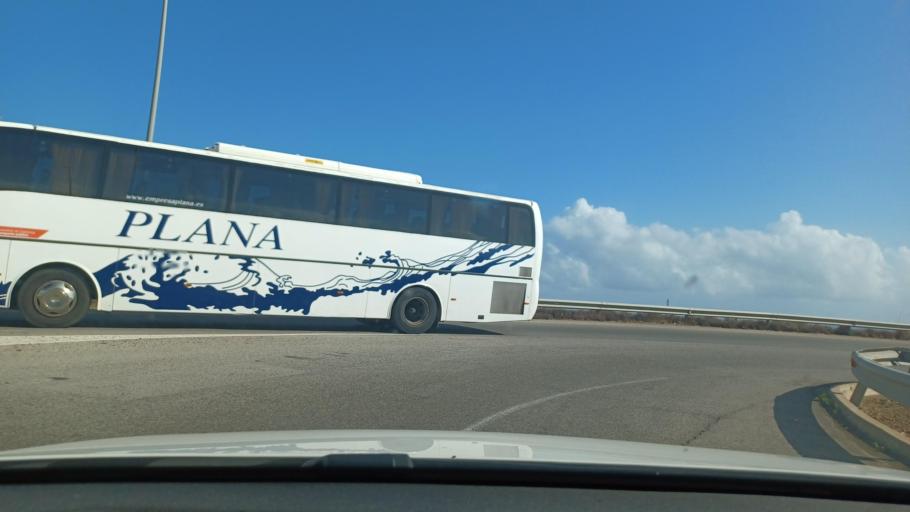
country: ES
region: Catalonia
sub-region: Provincia de Tarragona
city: Cambrils
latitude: 41.0835
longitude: 1.0775
